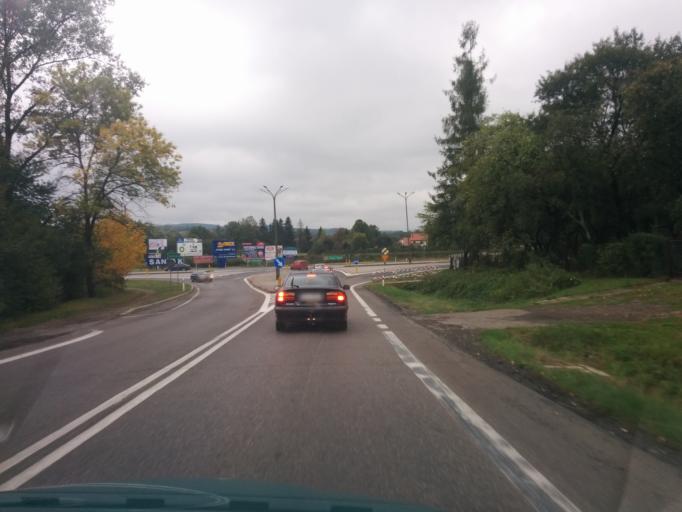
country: PL
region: Subcarpathian Voivodeship
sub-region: Powiat sanocki
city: Sanok
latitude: 49.5706
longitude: 22.1513
